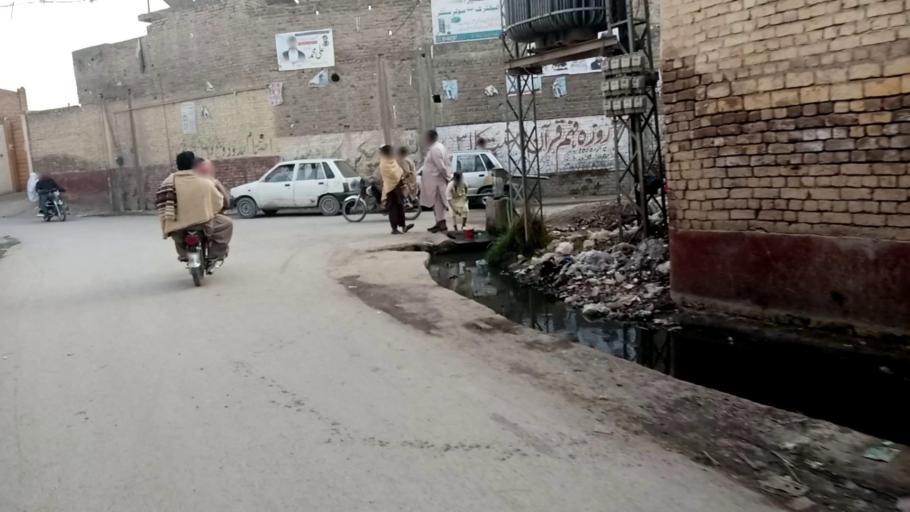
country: PK
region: Khyber Pakhtunkhwa
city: Peshawar
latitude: 34.0493
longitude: 71.4600
